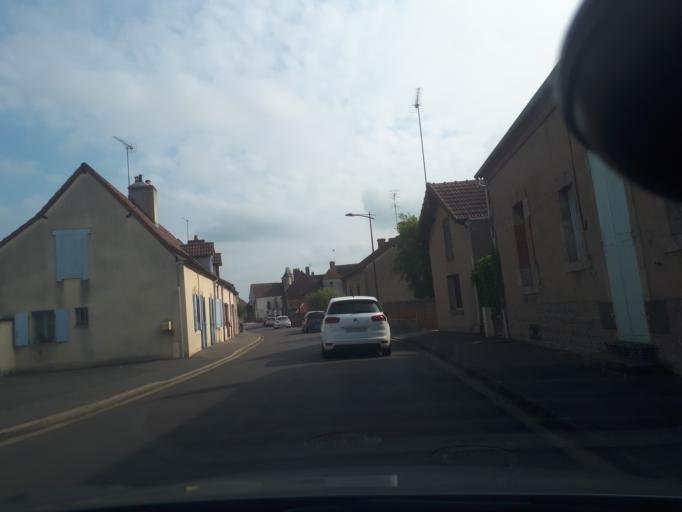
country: FR
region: Auvergne
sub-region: Departement de l'Allier
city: Dompierre-sur-Besbre
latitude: 46.4446
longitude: 3.6295
